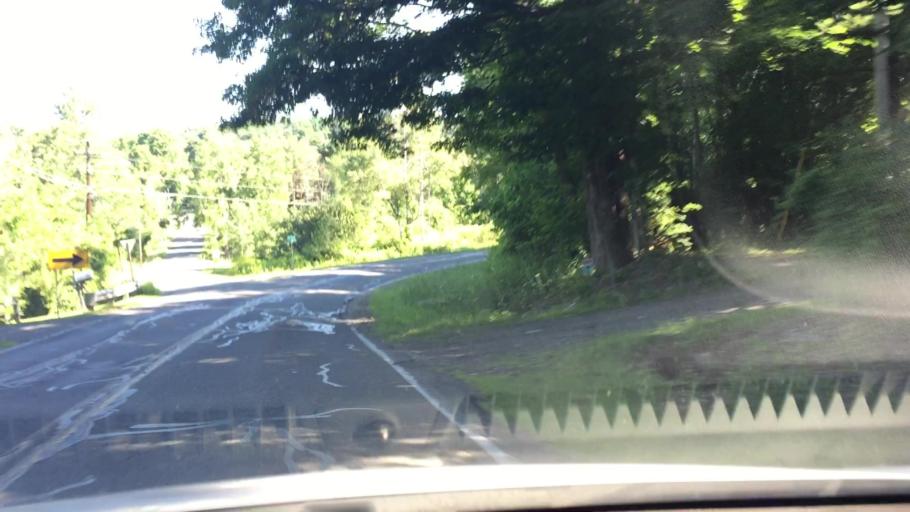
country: US
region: Massachusetts
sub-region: Berkshire County
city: West Stockbridge
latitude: 42.3468
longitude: -73.3651
